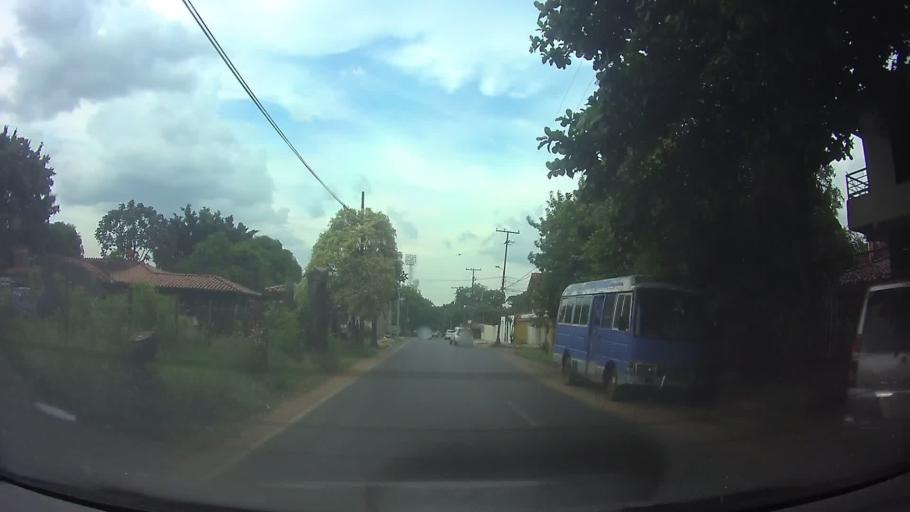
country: PY
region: Central
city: San Lorenzo
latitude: -25.2757
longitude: -57.4934
